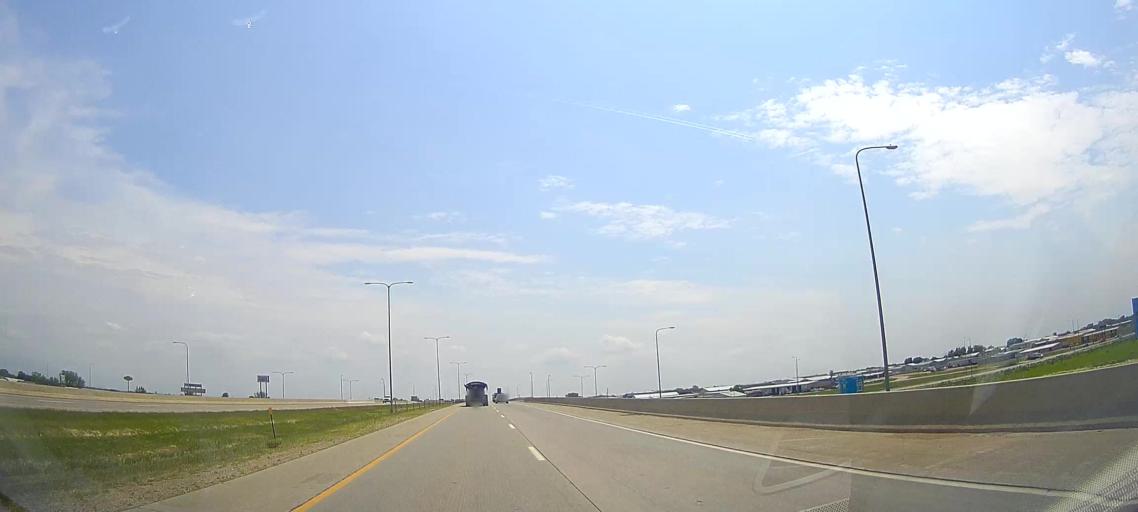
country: US
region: South Dakota
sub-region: Lincoln County
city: Tea
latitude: 43.4624
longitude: -96.7976
